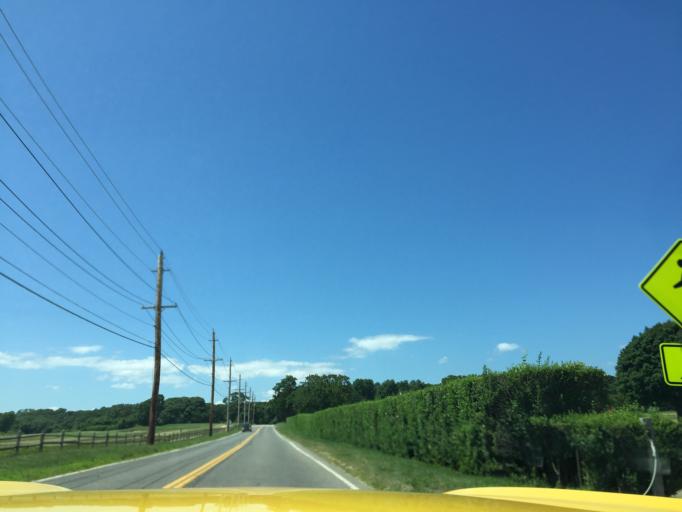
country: US
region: New York
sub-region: Suffolk County
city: Amagansett
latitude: 40.9821
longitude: -72.1326
